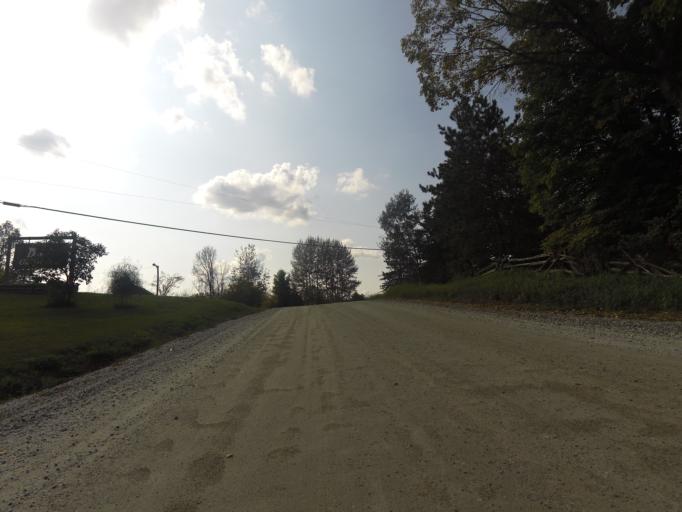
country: CA
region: Ontario
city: Renfrew
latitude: 45.1576
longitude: -76.6858
